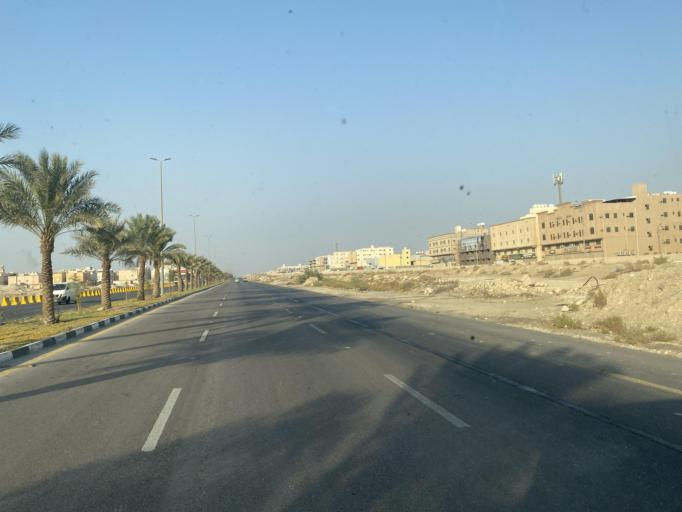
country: SA
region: Eastern Province
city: Dhahran
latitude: 26.3546
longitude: 50.0578
